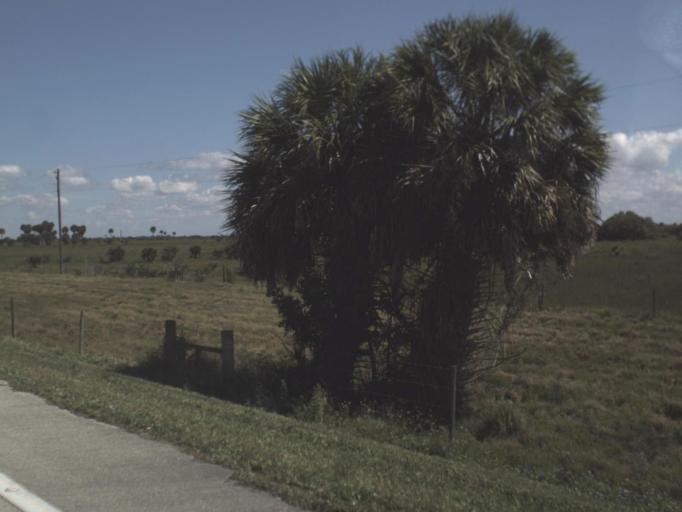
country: US
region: Florida
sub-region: Glades County
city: Buckhead Ridge
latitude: 27.0812
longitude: -80.9705
